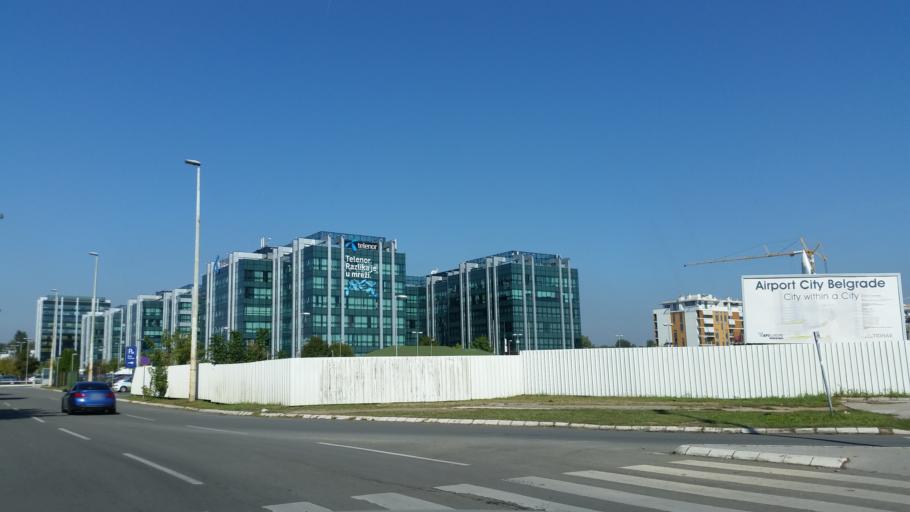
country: RS
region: Central Serbia
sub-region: Belgrade
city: Novi Beograd
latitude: 44.8101
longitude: 20.4002
